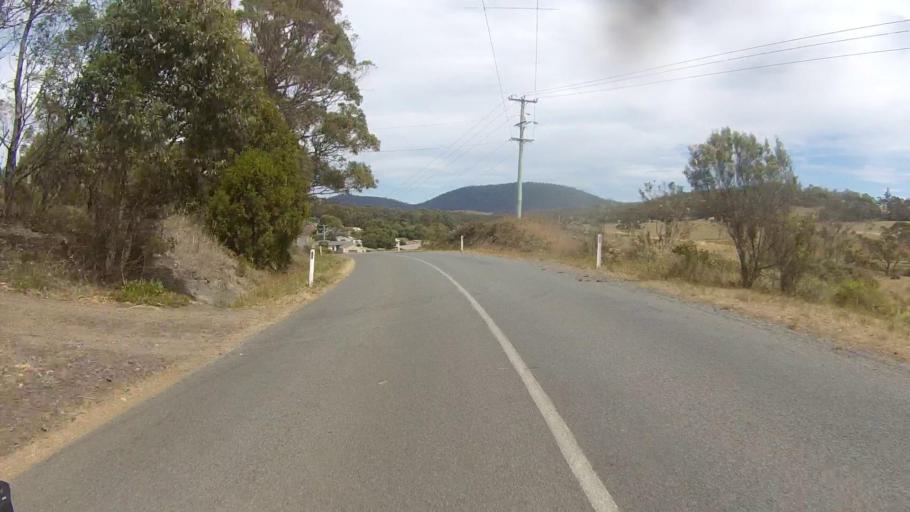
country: AU
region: Tasmania
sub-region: Sorell
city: Sorell
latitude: -42.8192
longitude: 147.8080
